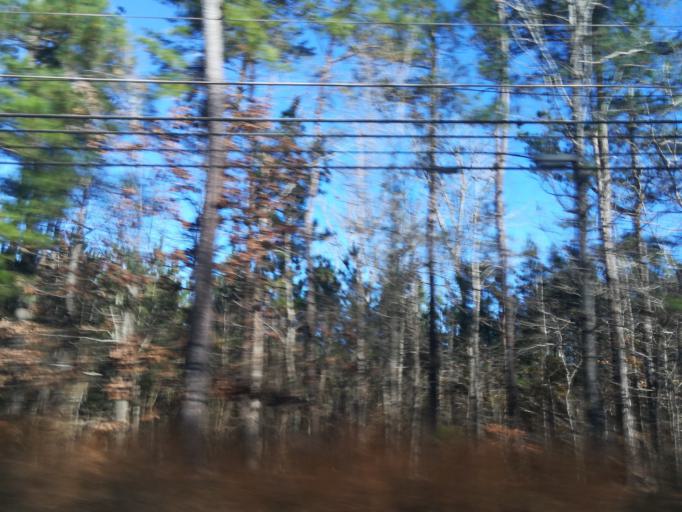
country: US
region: North Carolina
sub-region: Durham County
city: Durham
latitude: 36.0341
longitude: -78.9983
